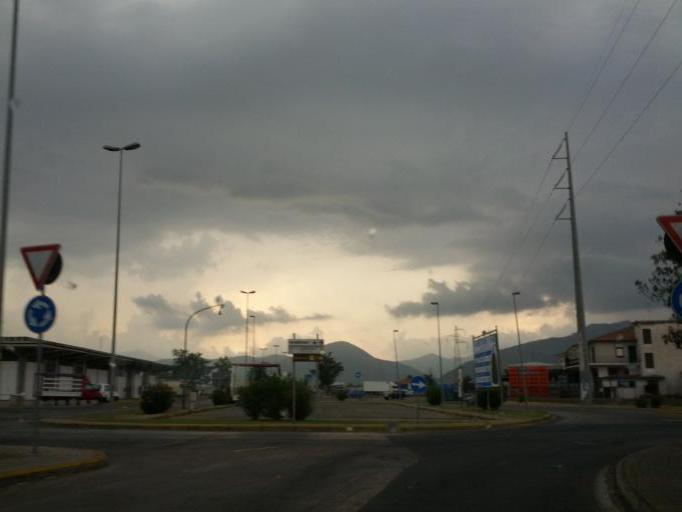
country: IT
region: Latium
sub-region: Provincia di Latina
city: Fondi
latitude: 41.3419
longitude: 13.4181
